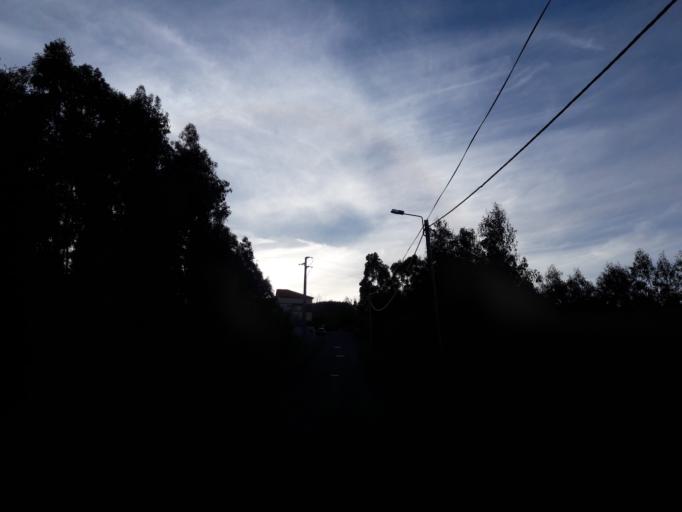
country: PT
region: Madeira
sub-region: Santa Cruz
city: Camacha
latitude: 32.6864
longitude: -16.8562
